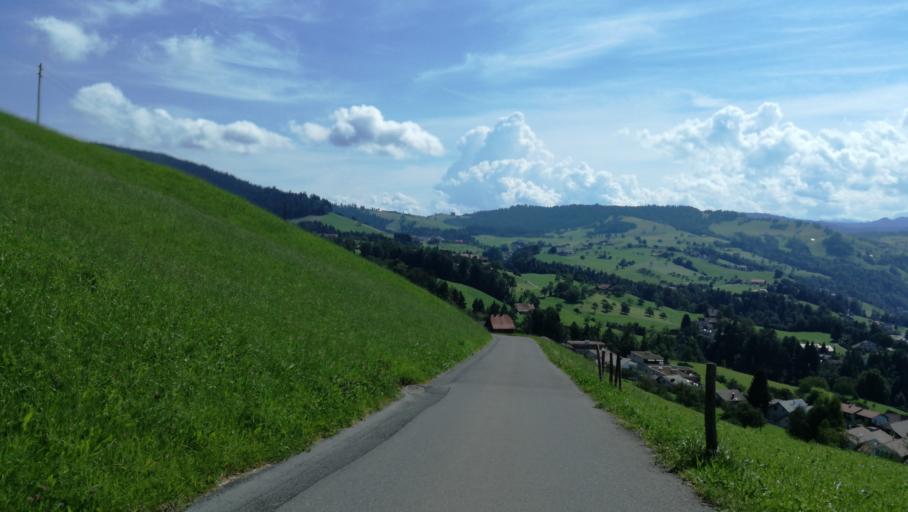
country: CH
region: Zug
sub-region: Zug
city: Unterageri
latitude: 47.1435
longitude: 8.6033
